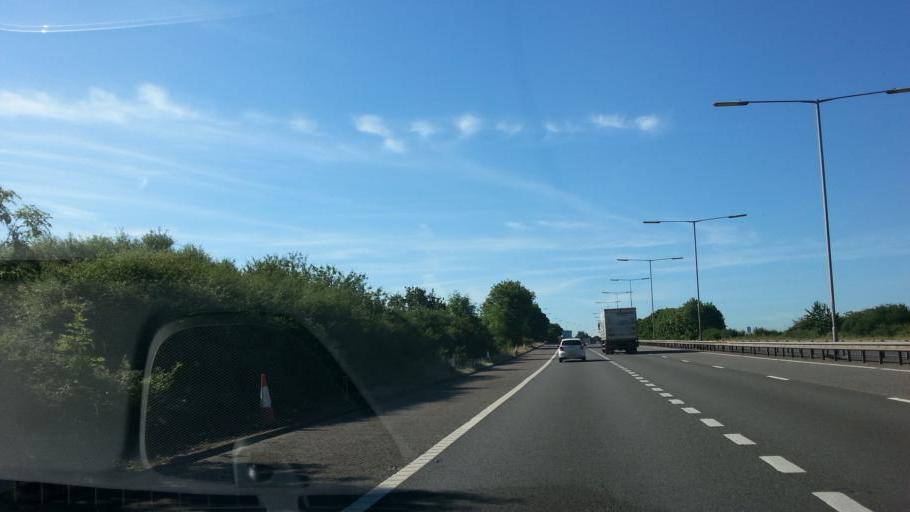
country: GB
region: England
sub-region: Warwickshire
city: Bedworth
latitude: 52.4410
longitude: -1.4247
